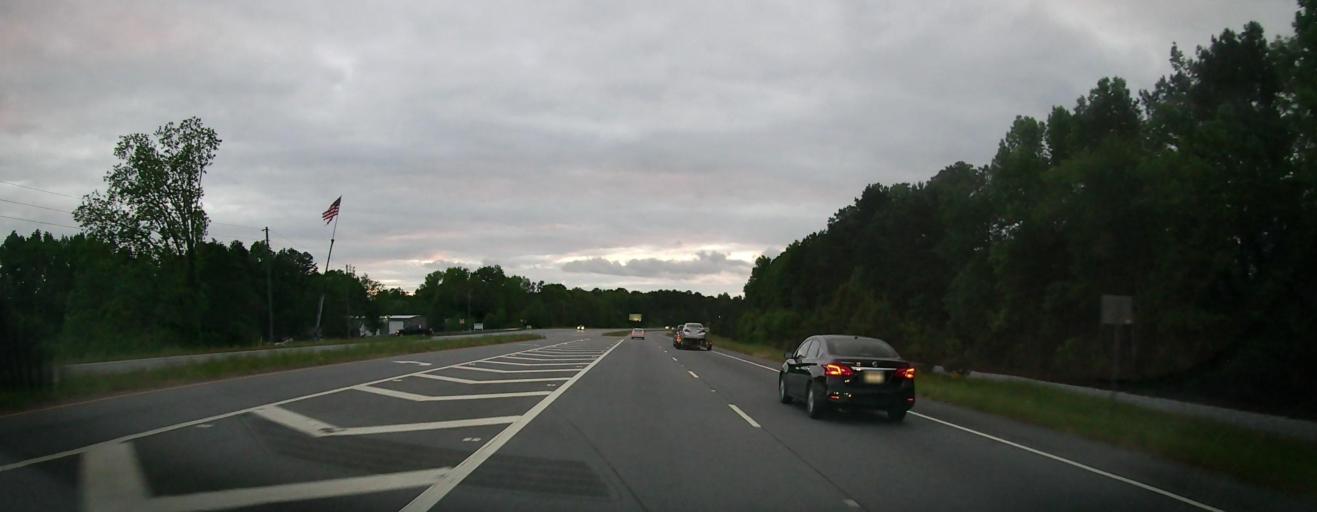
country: US
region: Georgia
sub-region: Jackson County
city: Arcade
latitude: 34.0656
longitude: -83.5428
